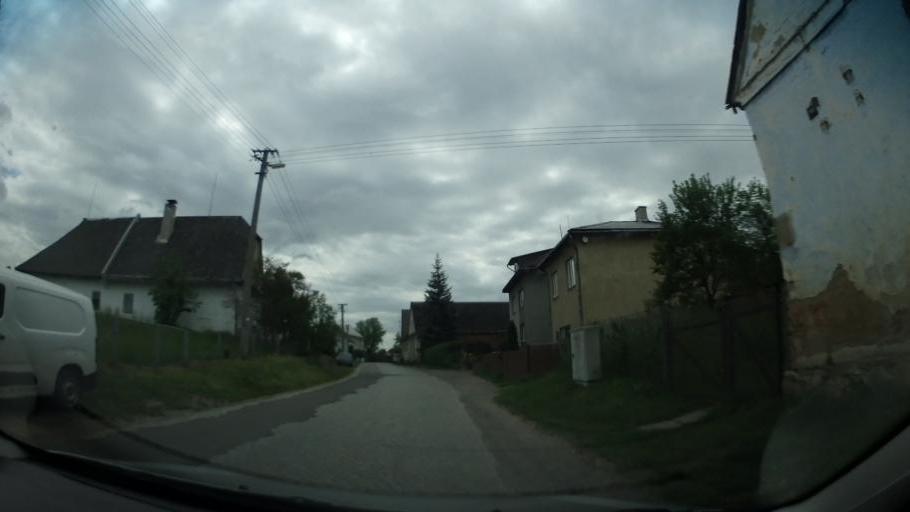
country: CZ
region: Pardubicky
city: Kuncina
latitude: 49.8449
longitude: 16.6973
